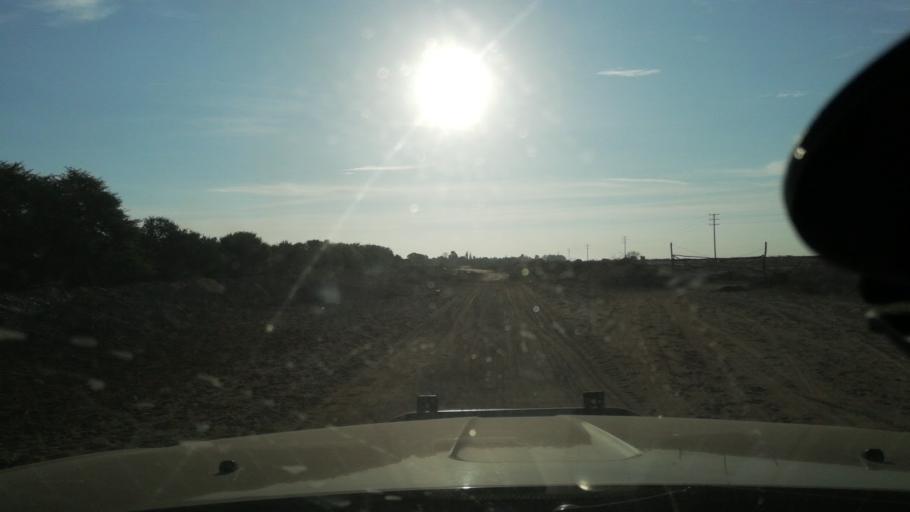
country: PE
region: Ica
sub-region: Provincia de Chincha
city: San Pedro
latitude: -13.3399
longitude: -76.1595
